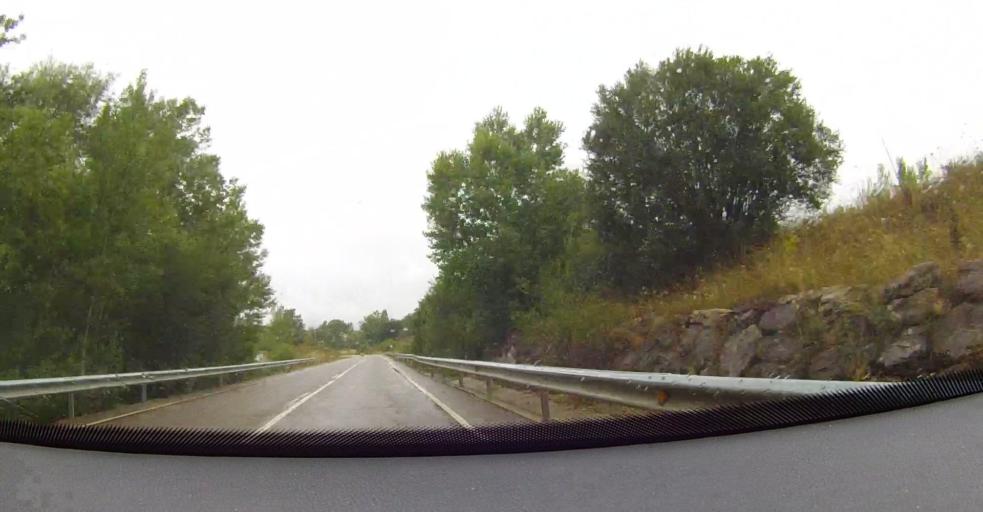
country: ES
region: Castille and Leon
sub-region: Provincia de Leon
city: Bonar
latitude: 42.8447
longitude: -5.2621
